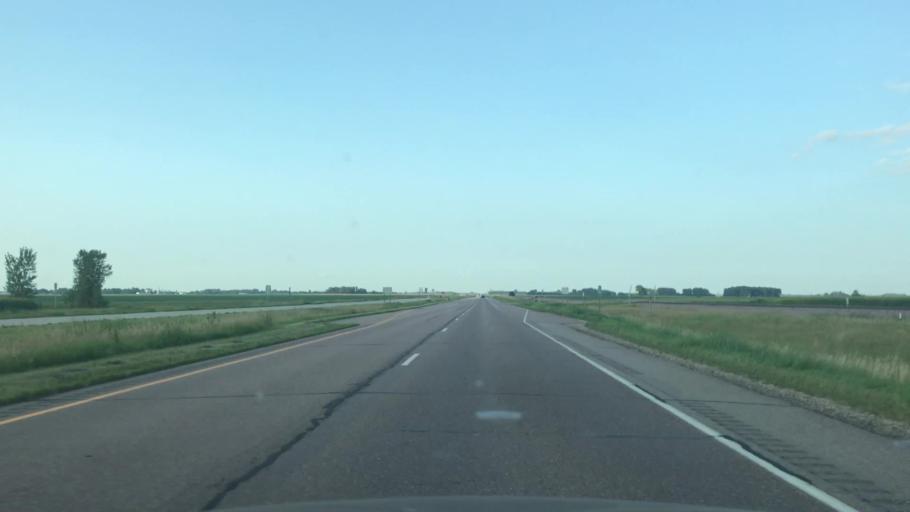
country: US
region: Minnesota
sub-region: Nobles County
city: Worthington
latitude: 43.7308
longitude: -95.4220
